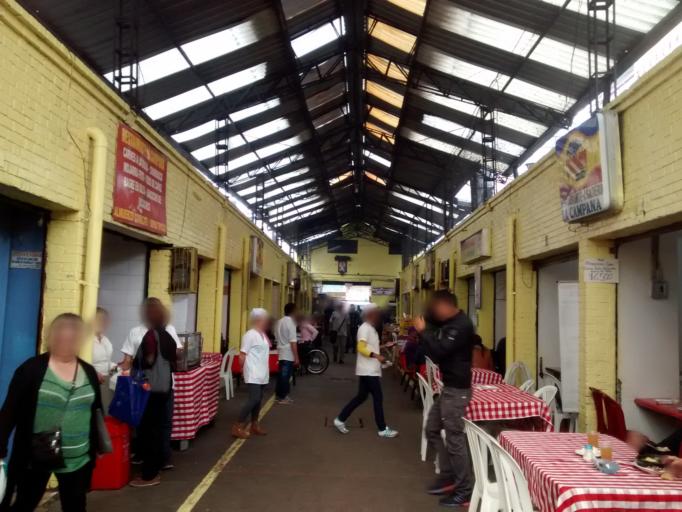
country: CO
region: Bogota D.C.
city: Bogota
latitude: 4.6066
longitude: -74.0723
